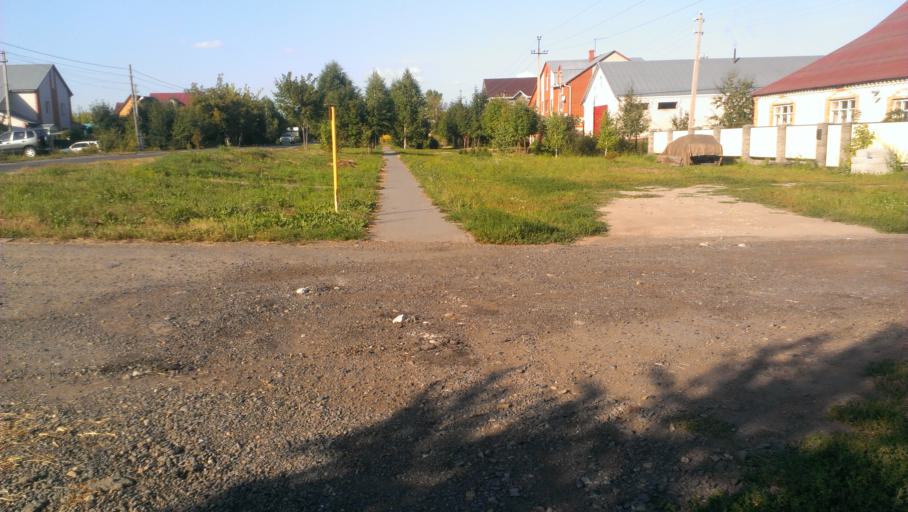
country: RU
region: Altai Krai
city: Novosilikatnyy
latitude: 53.3620
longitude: 83.6428
